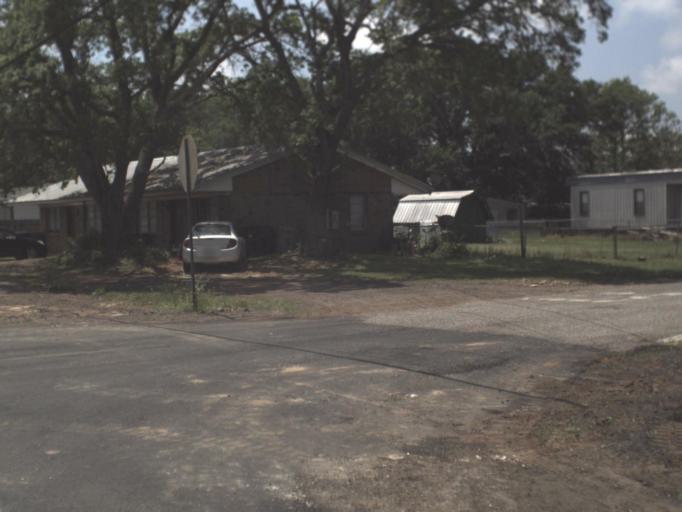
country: US
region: Florida
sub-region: Escambia County
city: Warrington
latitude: 30.3868
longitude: -87.3078
